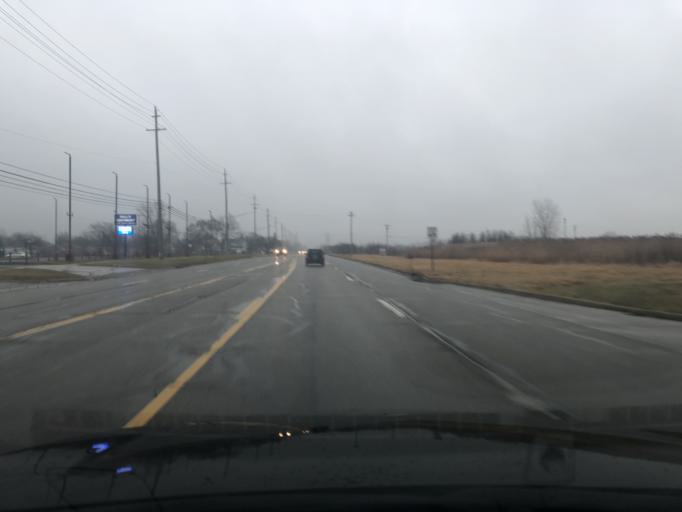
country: US
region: Michigan
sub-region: Wayne County
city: Woodhaven
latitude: 42.1253
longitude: -83.2258
